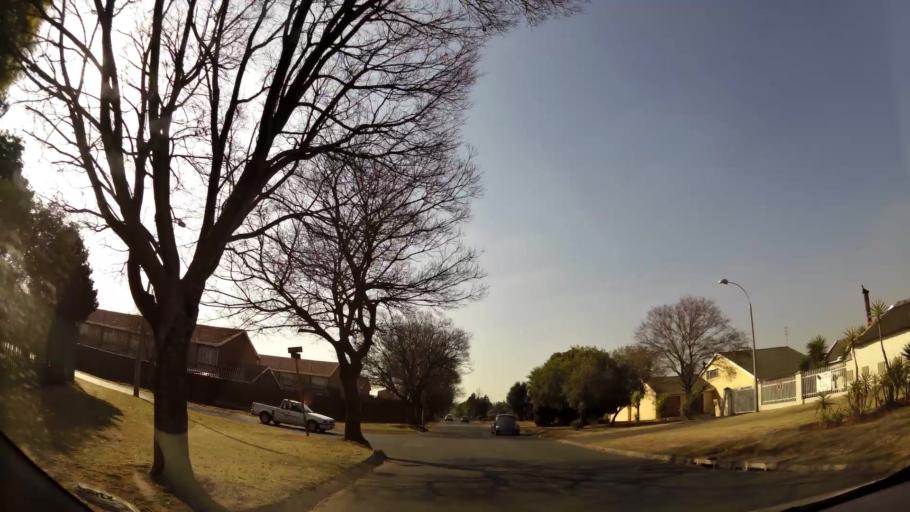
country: ZA
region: Gauteng
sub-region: West Rand District Municipality
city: Randfontein
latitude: -26.1811
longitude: 27.6861
